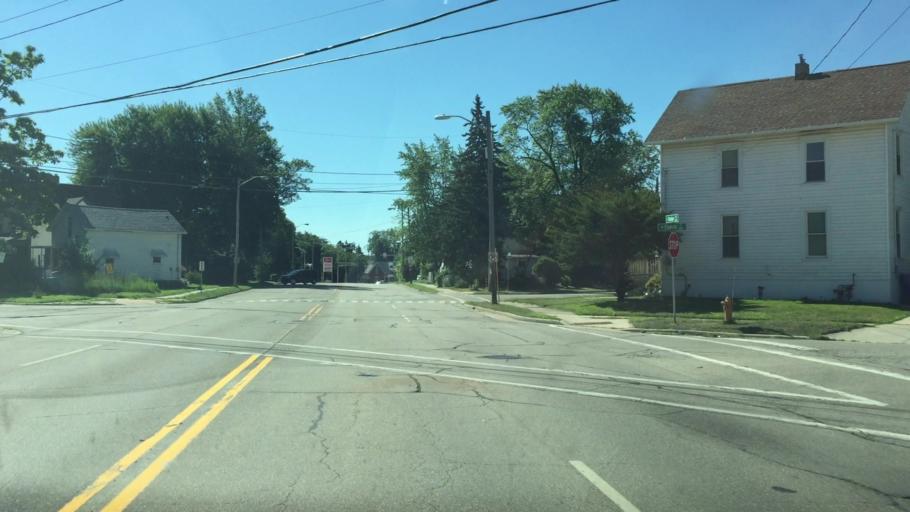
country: US
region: Wisconsin
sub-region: Outagamie County
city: Appleton
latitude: 44.2598
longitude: -88.4179
